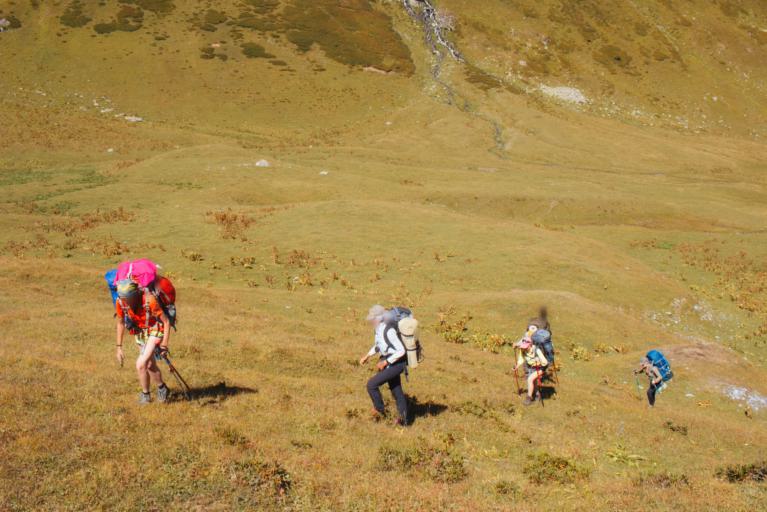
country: RU
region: Karachayevo-Cherkesiya
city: Mednogorskiy
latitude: 43.6108
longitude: 41.1531
